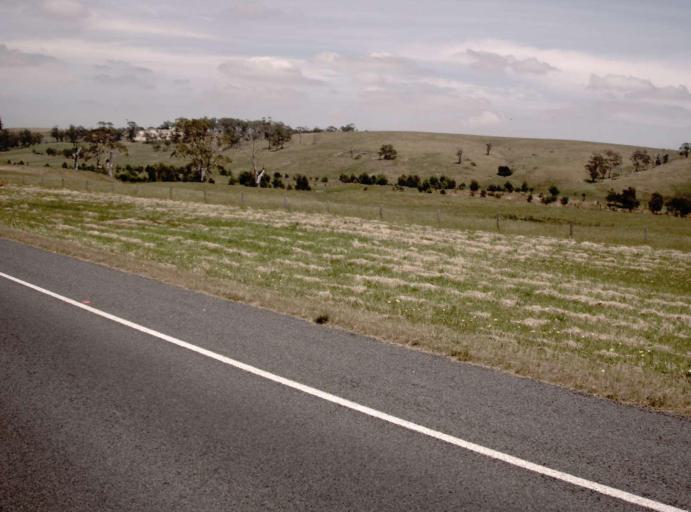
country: AU
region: Victoria
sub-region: Latrobe
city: Traralgon
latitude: -38.2292
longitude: 146.5409
